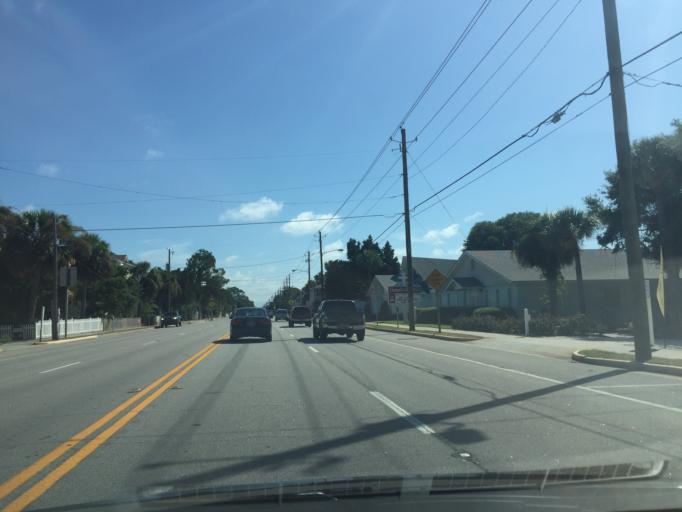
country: US
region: Georgia
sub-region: Chatham County
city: Tybee Island
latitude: 32.0033
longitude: -80.8449
